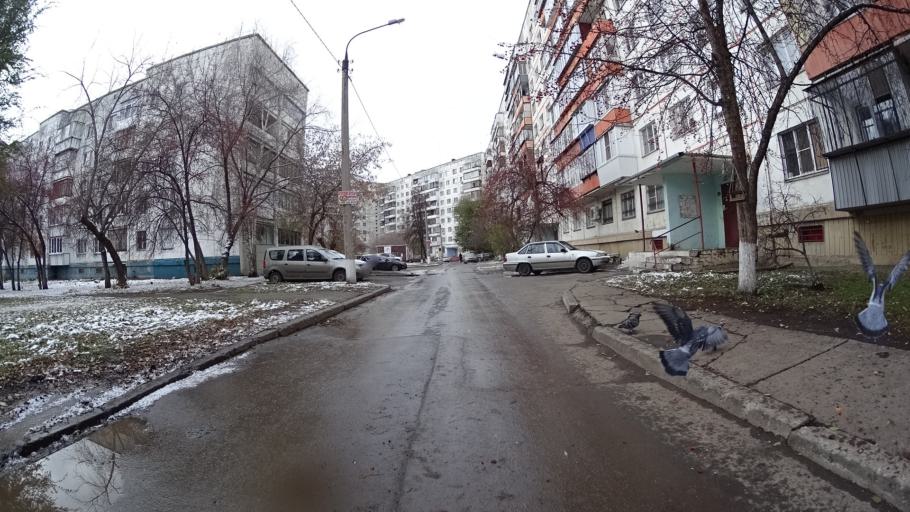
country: RU
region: Chelyabinsk
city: Roshchino
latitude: 55.1938
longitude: 61.3057
